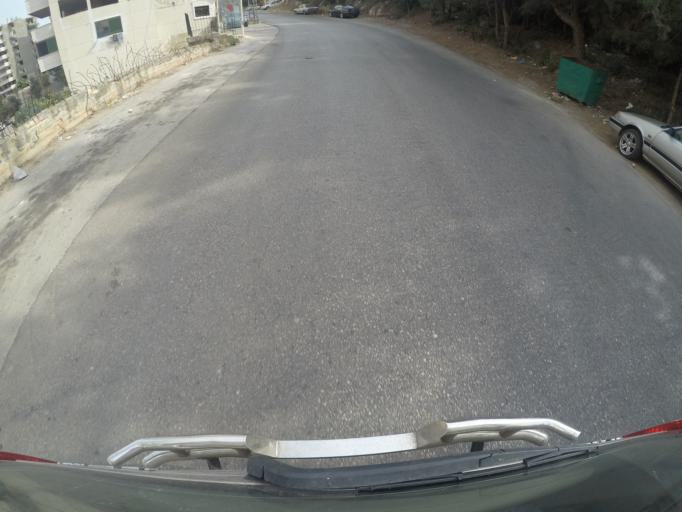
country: LB
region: Mont-Liban
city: Beit ed Dine
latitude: 33.7357
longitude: 35.4904
